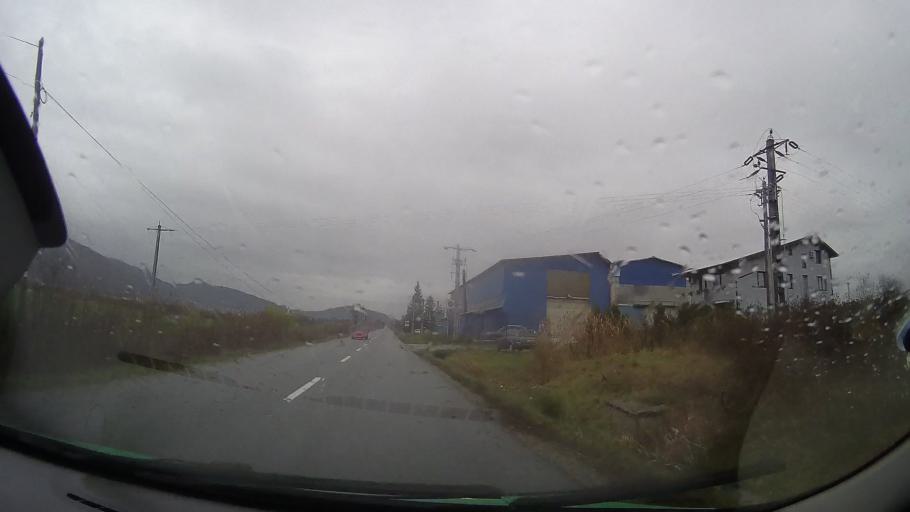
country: RO
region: Bistrita-Nasaud
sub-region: Municipiul Bistrita
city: Viisoara
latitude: 47.0602
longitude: 24.4360
